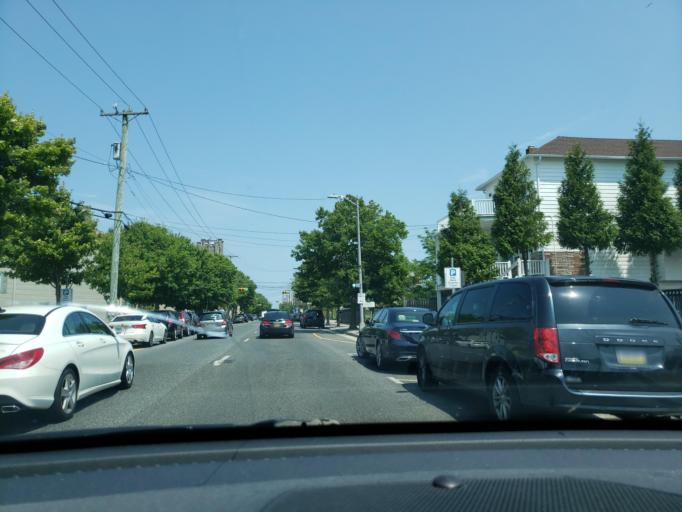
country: US
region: New Jersey
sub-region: Atlantic County
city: Atlantic City
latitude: 39.3613
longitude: -74.4349
